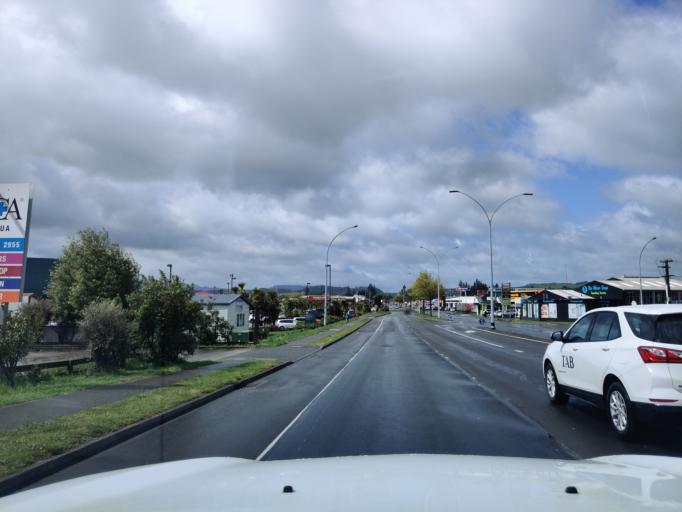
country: NZ
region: Bay of Plenty
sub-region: Rotorua District
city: Rotorua
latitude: -38.1277
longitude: 176.2325
